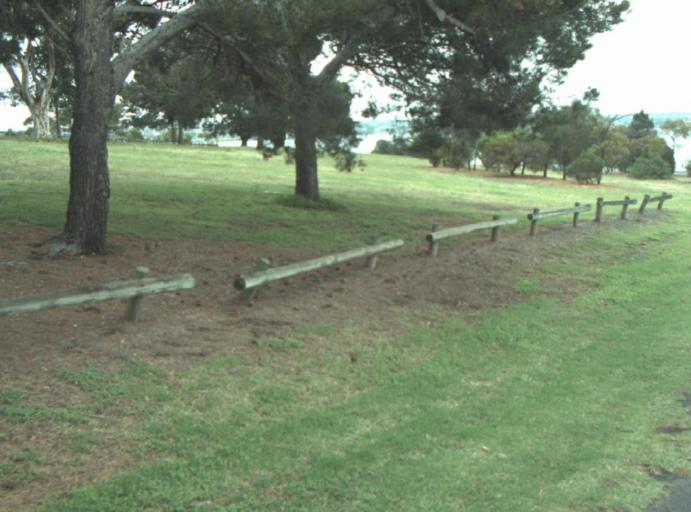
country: AU
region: Victoria
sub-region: Greater Geelong
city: East Geelong
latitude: -38.1456
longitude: 144.3850
